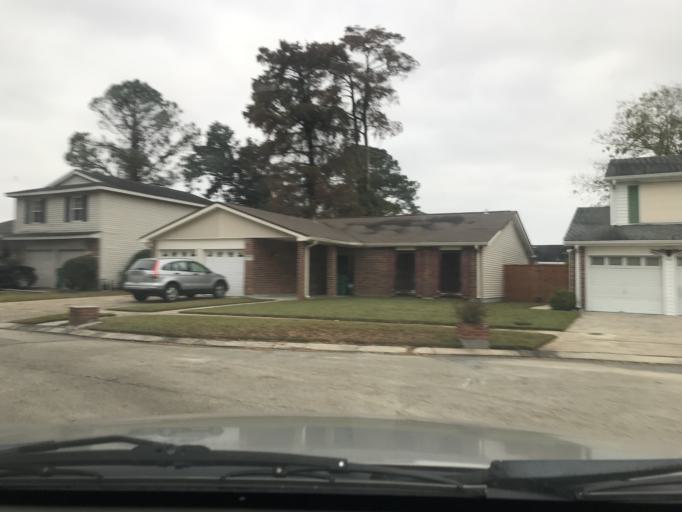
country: US
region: Louisiana
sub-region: Jefferson Parish
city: Woodmere
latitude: 29.8633
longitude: -90.0772
